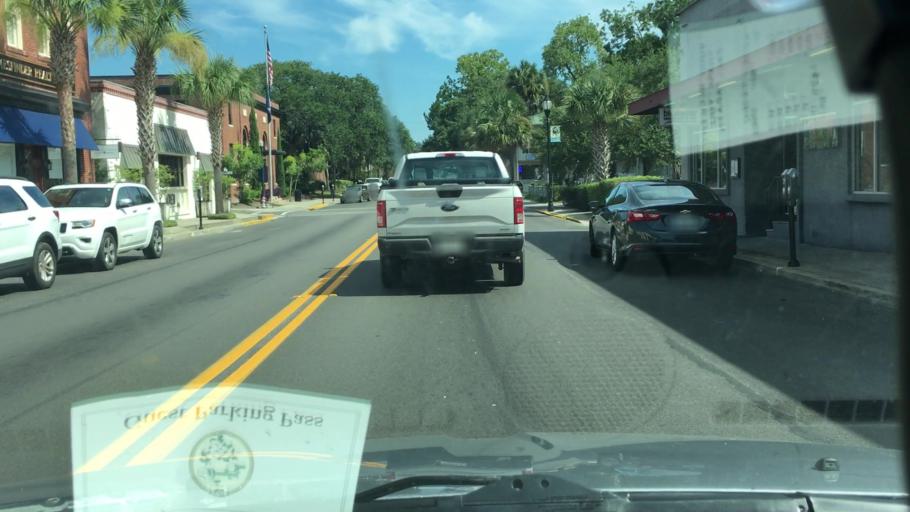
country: US
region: South Carolina
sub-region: Beaufort County
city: Beaufort
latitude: 32.4312
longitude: -80.6700
